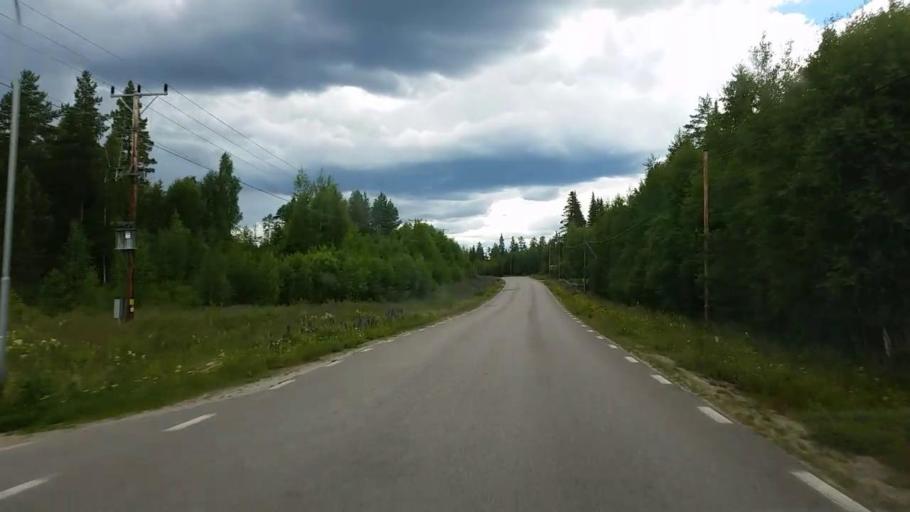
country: SE
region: Gaevleborg
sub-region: Ovanakers Kommun
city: Edsbyn
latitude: 61.4579
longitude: 15.8758
